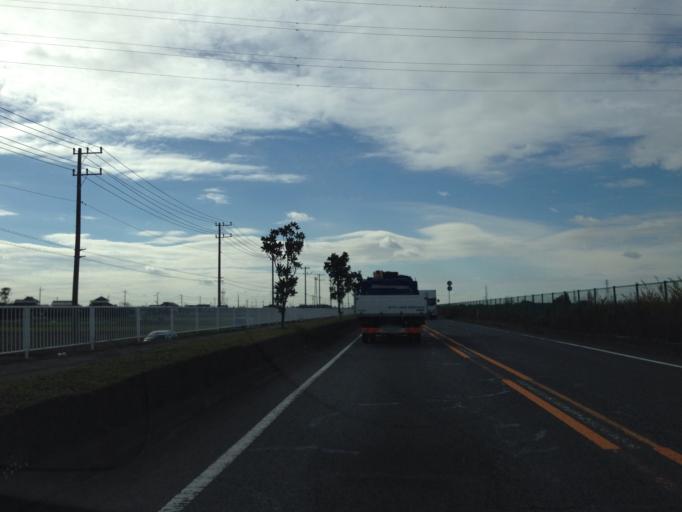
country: JP
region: Ibaraki
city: Fujishiro
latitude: 35.9320
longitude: 140.1213
